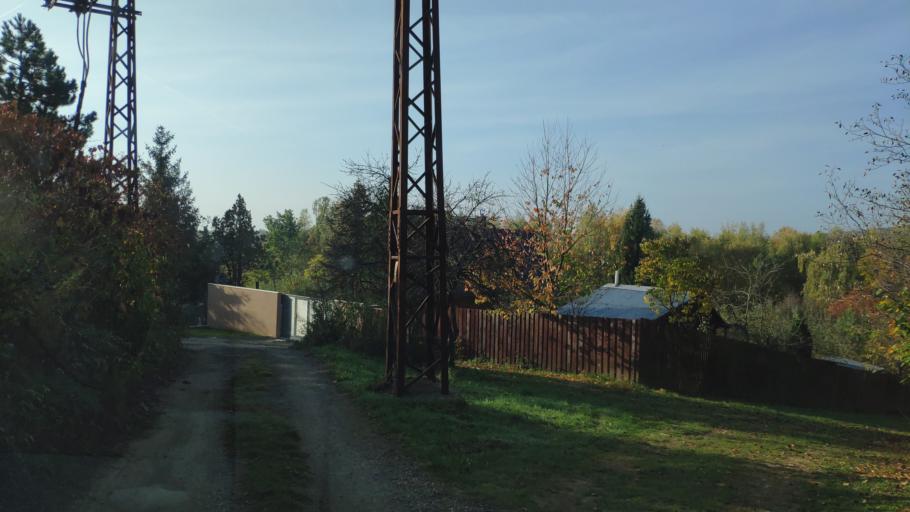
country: SK
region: Kosicky
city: Kosice
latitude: 48.7427
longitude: 21.2179
